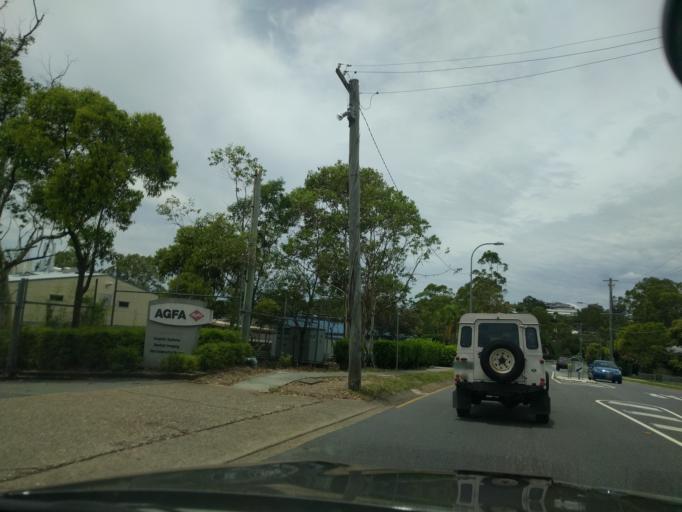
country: AU
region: Queensland
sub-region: Brisbane
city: Stafford
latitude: -27.4112
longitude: 153.0074
